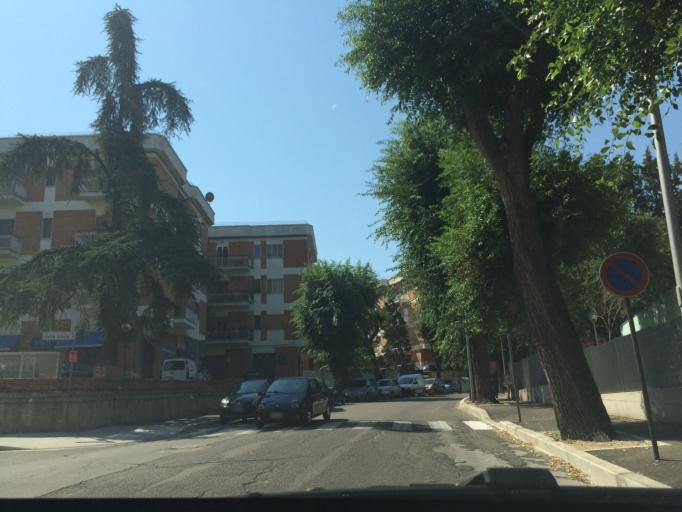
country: IT
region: Basilicate
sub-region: Provincia di Matera
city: Matera
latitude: 40.6730
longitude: 16.5985
